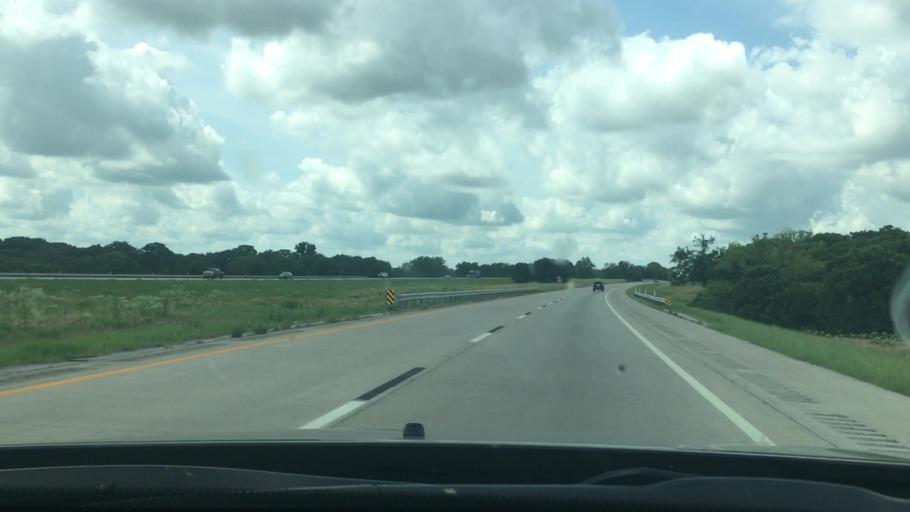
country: US
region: Oklahoma
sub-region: Love County
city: Marietta
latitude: 33.8230
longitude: -97.1307
